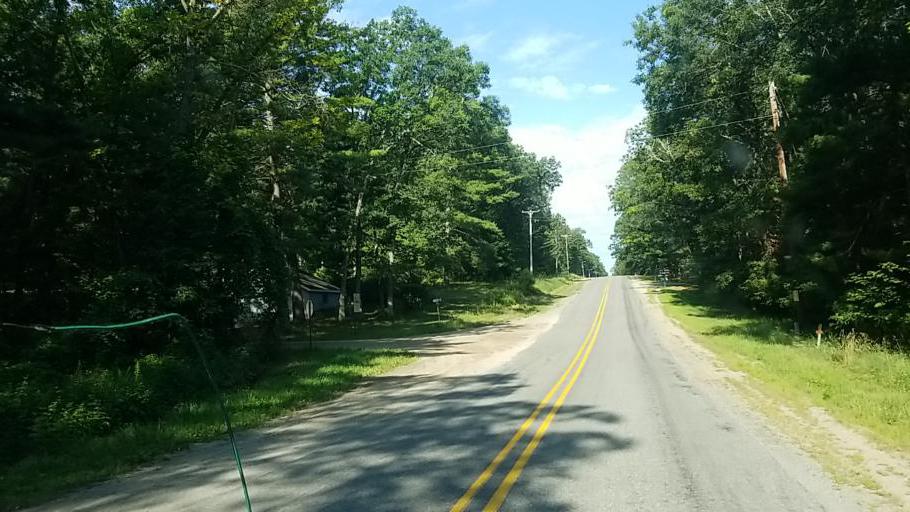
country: US
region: Michigan
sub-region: Muskegon County
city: Twin Lake
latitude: 43.4621
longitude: -86.2038
